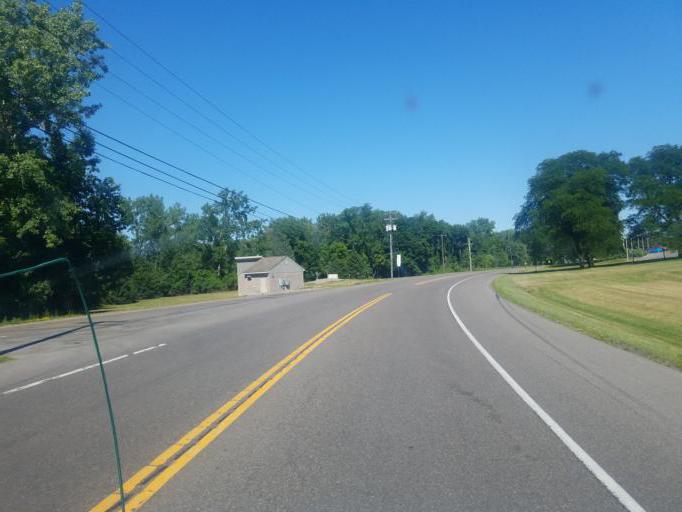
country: US
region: New York
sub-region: Wayne County
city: Lyons
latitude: 43.0679
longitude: -77.0349
